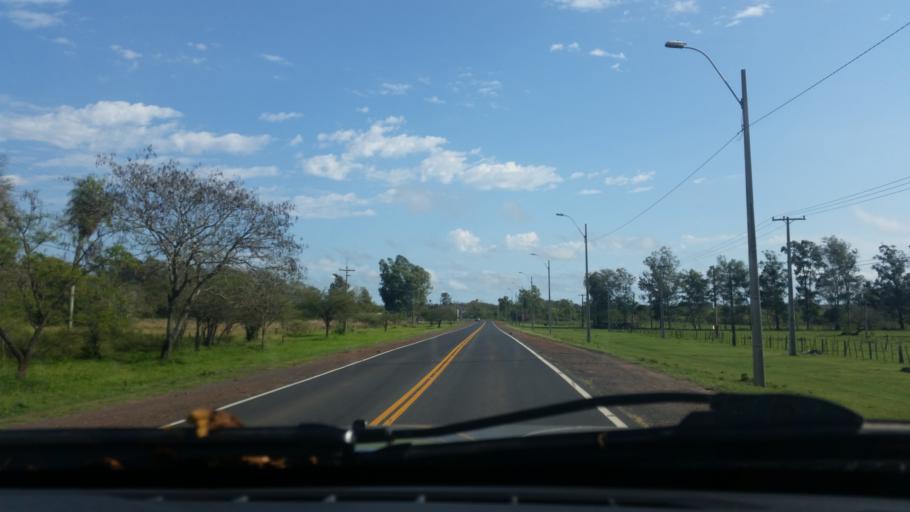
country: PY
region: Presidente Hayes
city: Villa Hayes
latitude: -25.0596
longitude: -57.5348
